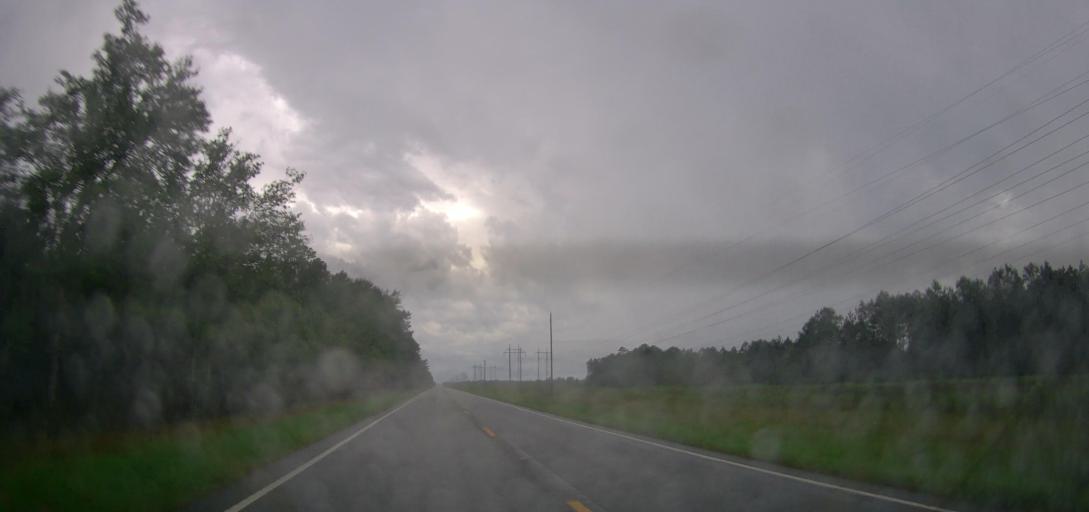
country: US
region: Georgia
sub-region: Brantley County
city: Nahunta
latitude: 31.3395
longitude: -81.8471
